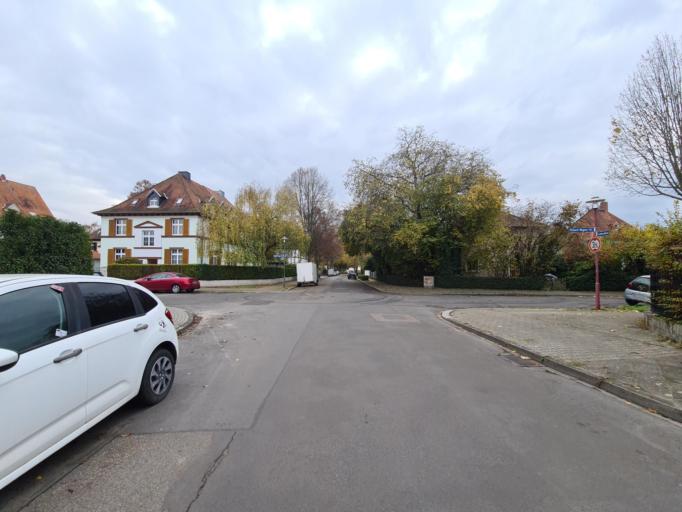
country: DE
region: Rheinland-Pfalz
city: Worms
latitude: 49.6341
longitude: 8.3363
